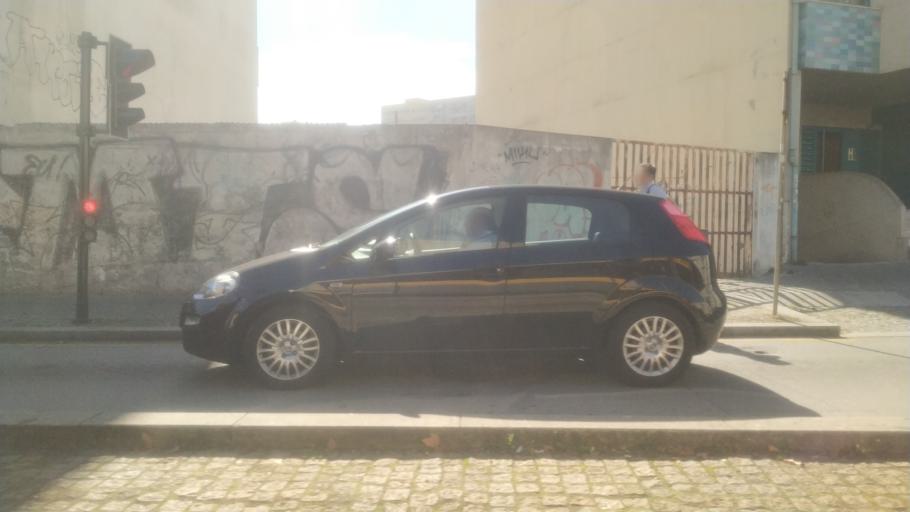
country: PT
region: Porto
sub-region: Matosinhos
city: Matosinhos
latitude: 41.1800
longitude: -8.6793
